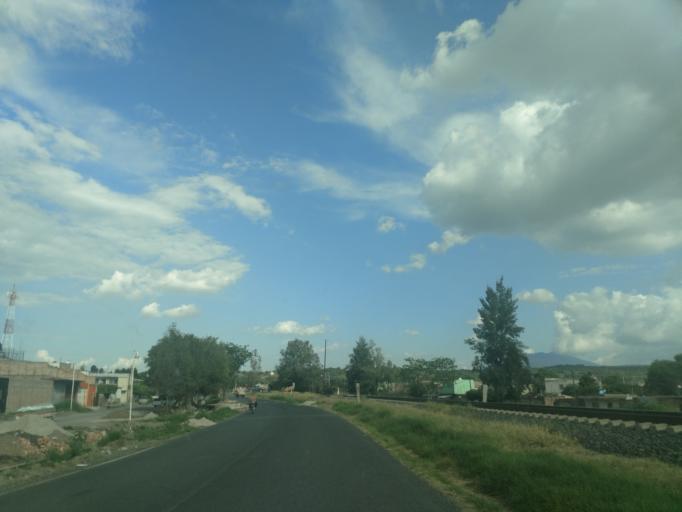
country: MX
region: Jalisco
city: Antonio Escobedo
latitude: 20.9053
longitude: -103.9845
